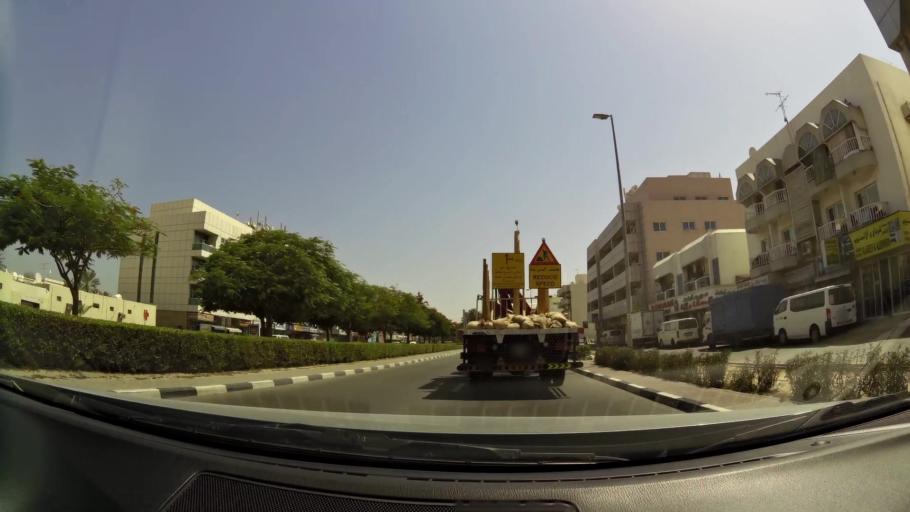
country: AE
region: Ash Shariqah
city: Sharjah
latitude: 25.2255
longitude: 55.2727
